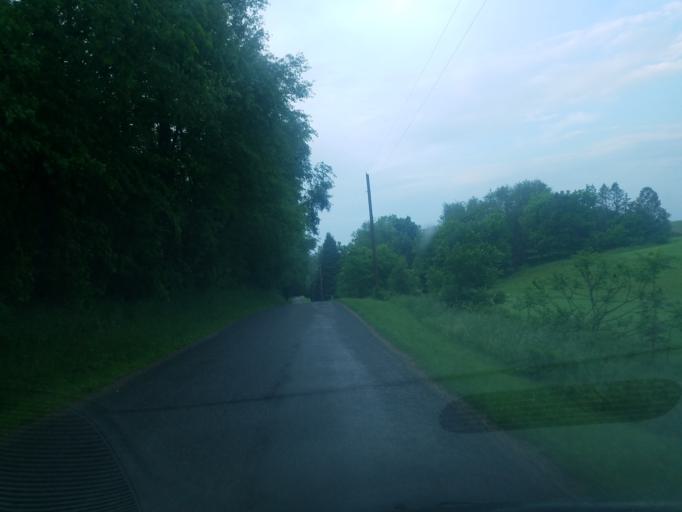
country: US
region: Ohio
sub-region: Stark County
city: Minerva
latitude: 40.7695
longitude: -80.9557
